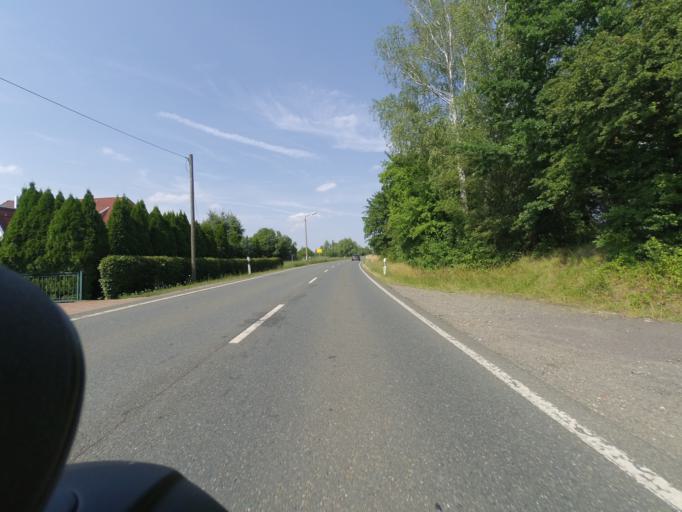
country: DE
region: Thuringia
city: Meuselwitz
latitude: 51.0653
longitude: 12.3139
